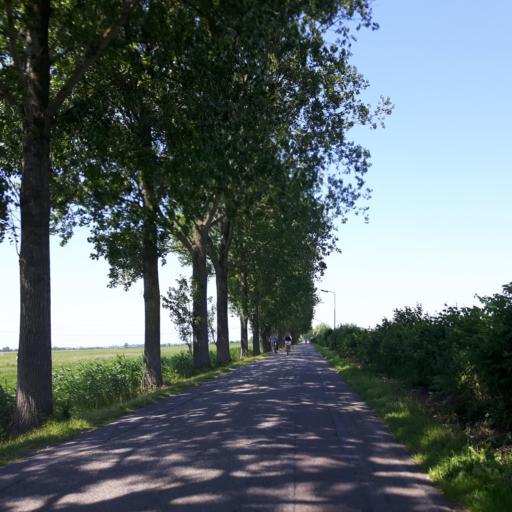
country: NL
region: Utrecht
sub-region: Stichtse Vecht
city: Spechtenkamp
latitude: 52.1246
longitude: 4.9684
